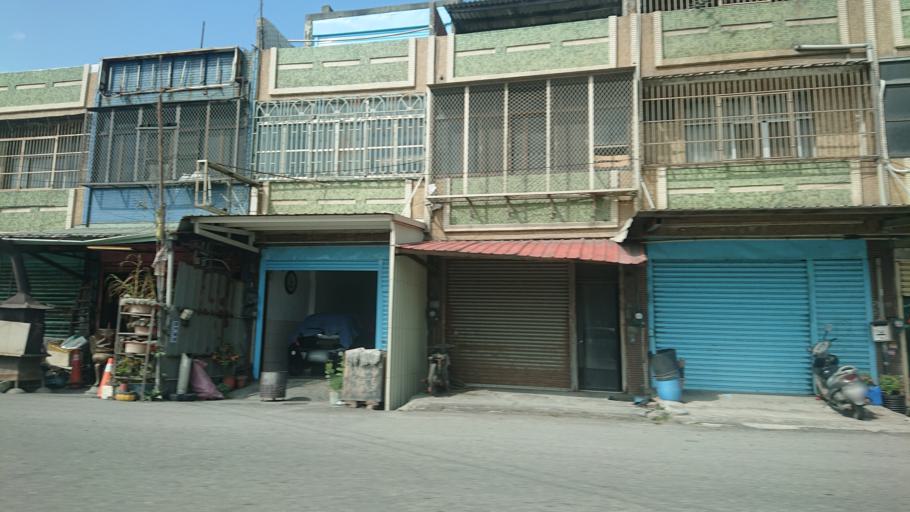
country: TW
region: Taiwan
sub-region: Changhua
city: Chang-hua
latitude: 23.9316
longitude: 120.3216
